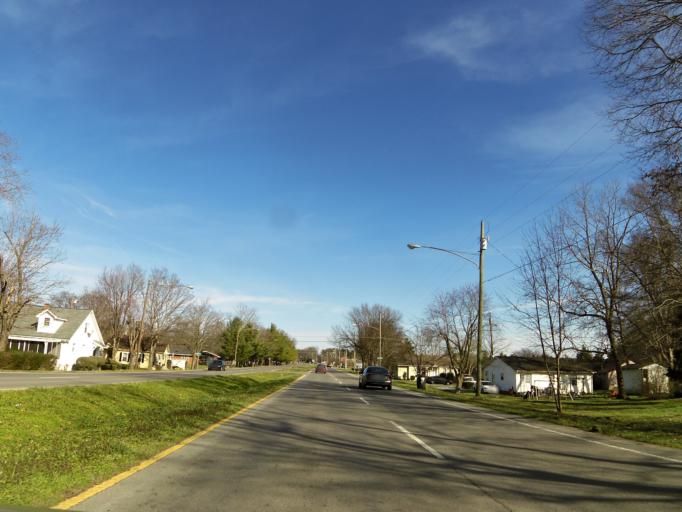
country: US
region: Tennessee
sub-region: Rutherford County
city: Murfreesboro
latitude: 35.8371
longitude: -86.3801
